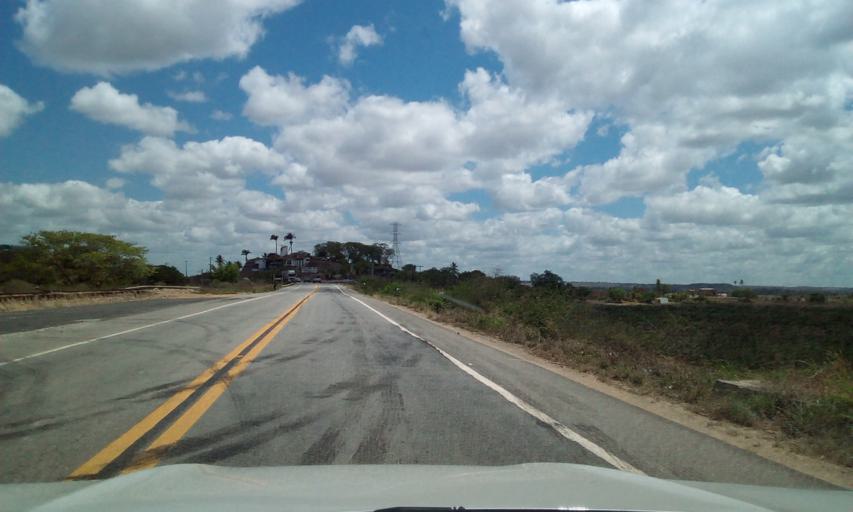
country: BR
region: Sergipe
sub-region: Propria
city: Propria
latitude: -10.2183
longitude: -36.8256
